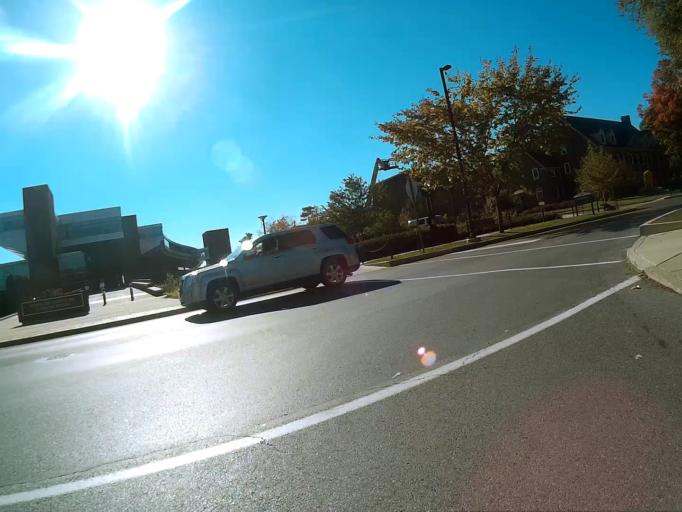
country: US
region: Pennsylvania
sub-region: Centre County
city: State College
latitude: 40.7953
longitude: -77.8665
